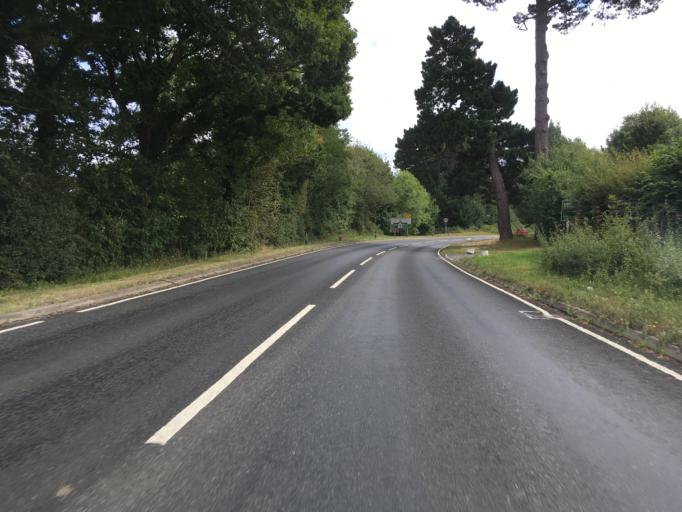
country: GB
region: England
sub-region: Kent
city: Cranbrook
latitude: 51.1096
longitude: 0.5432
